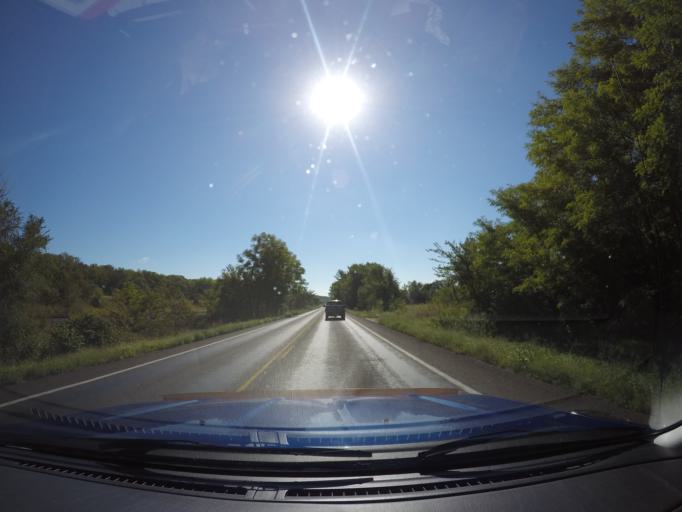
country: US
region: Kansas
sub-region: Pottawatomie County
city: Saint Marys
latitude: 39.1826
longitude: -96.0406
